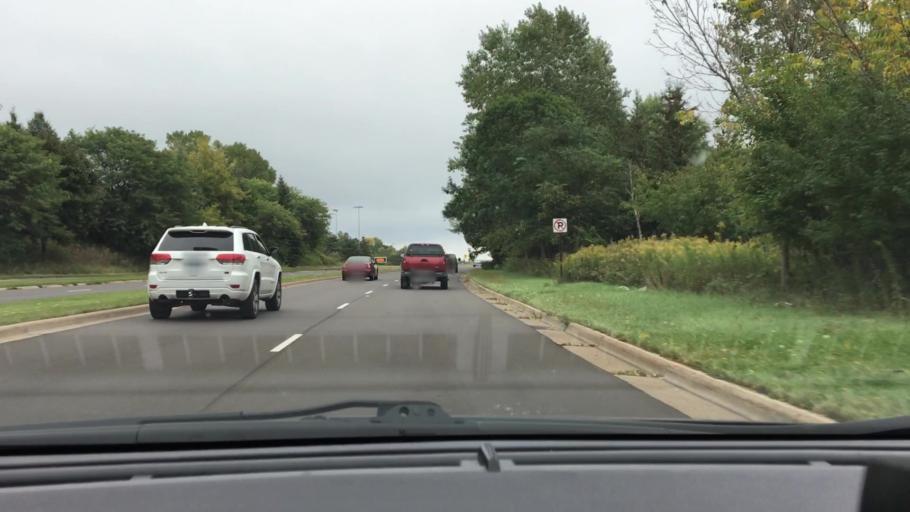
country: US
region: Minnesota
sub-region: Hennepin County
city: Plymouth
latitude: 45.0335
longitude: -93.4278
